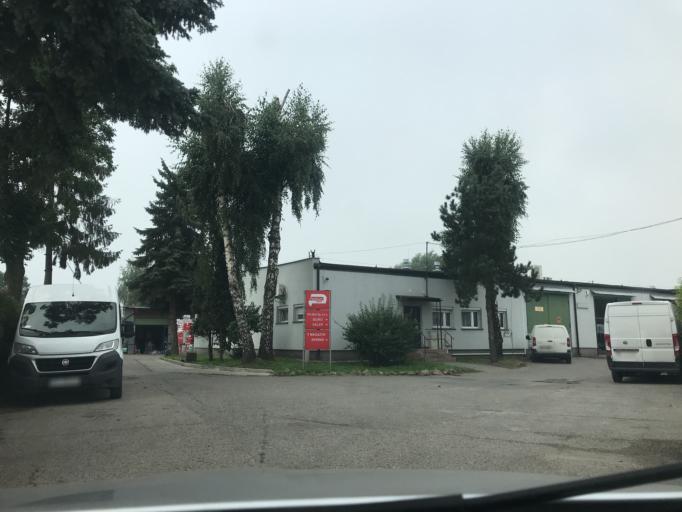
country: PL
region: Lesser Poland Voivodeship
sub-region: Powiat krakowski
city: Ochojno
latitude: 50.0067
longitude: 19.9733
